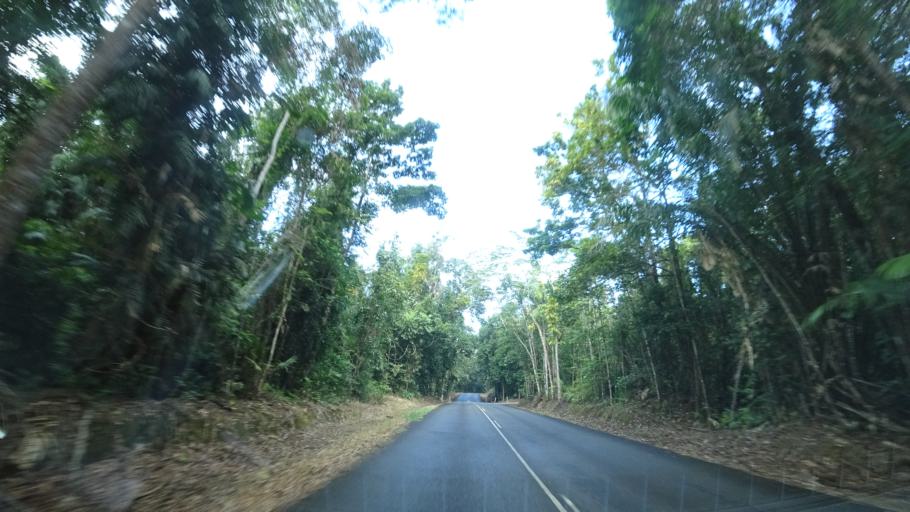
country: AU
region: Queensland
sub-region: Cairns
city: Port Douglas
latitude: -16.1827
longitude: 145.4144
